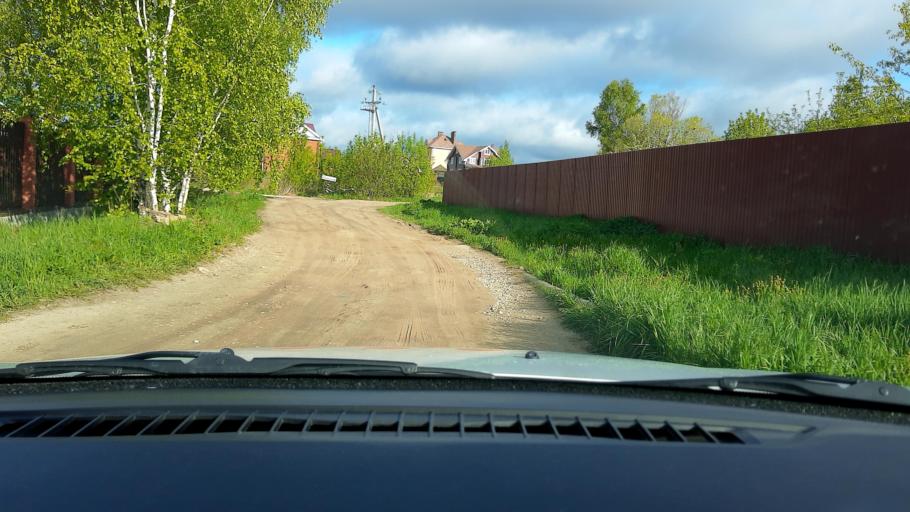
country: RU
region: Nizjnij Novgorod
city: Afonino
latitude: 56.1932
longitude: 44.0710
